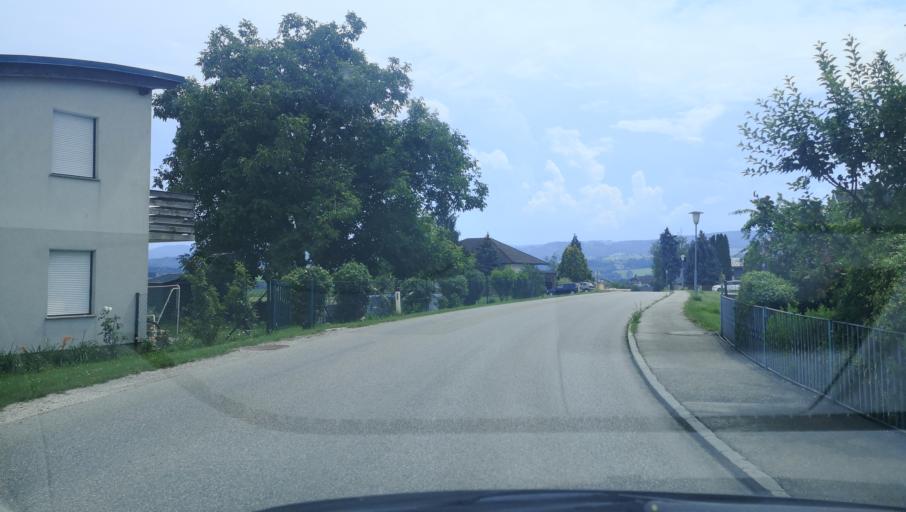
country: AT
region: Lower Austria
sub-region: Politischer Bezirk Amstetten
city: Ferschnitz
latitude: 48.1000
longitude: 14.9791
